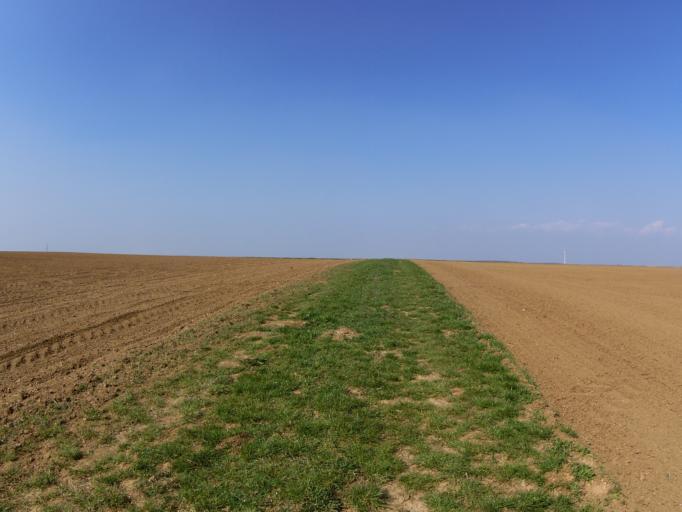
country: DE
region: Bavaria
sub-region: Regierungsbezirk Unterfranken
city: Mainstockheim
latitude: 49.7899
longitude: 10.1413
